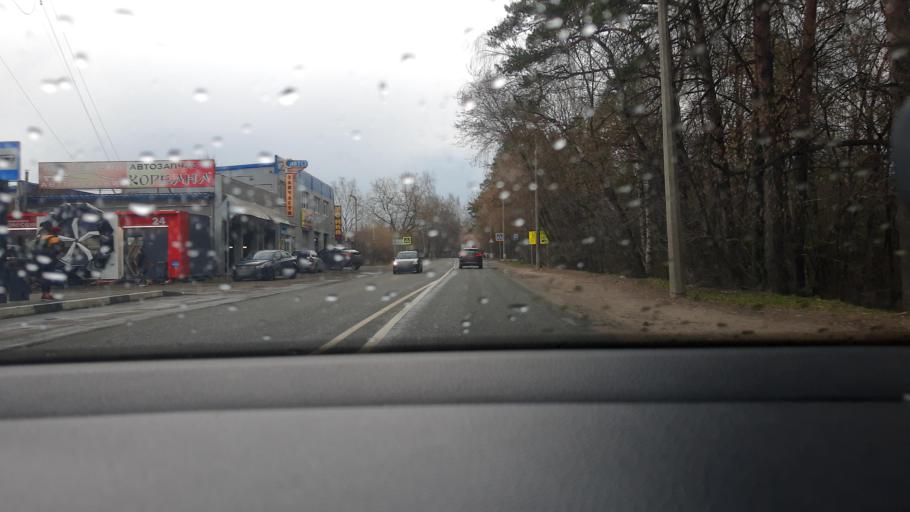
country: RU
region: Moskovskaya
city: Bolshevo
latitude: 55.9350
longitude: 37.8289
